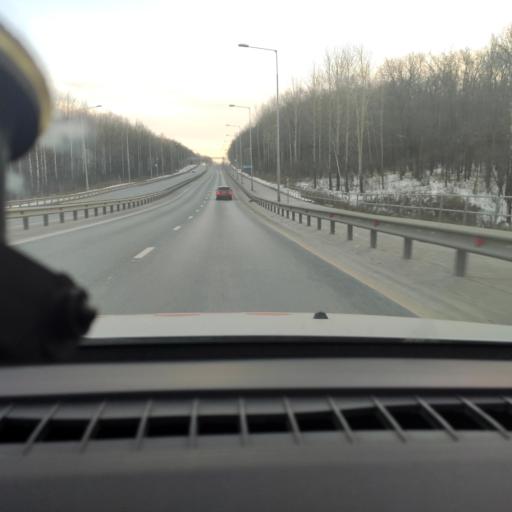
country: RU
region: Samara
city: Petra-Dubrava
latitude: 53.2896
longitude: 50.2484
